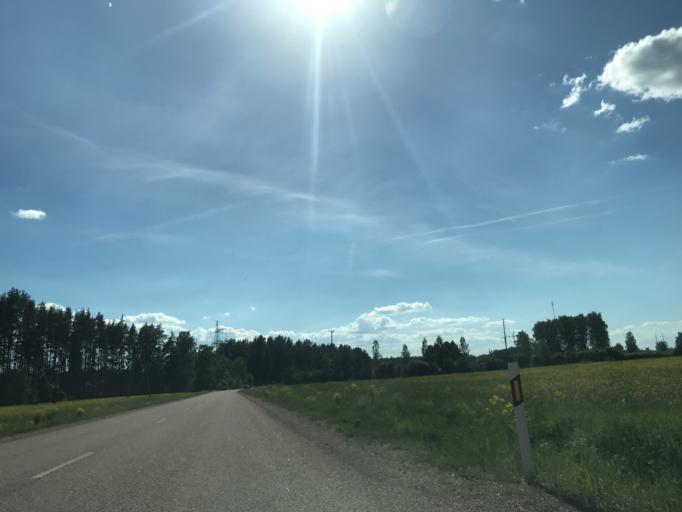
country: LV
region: Koknese
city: Koknese
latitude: 56.5665
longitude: 25.5131
